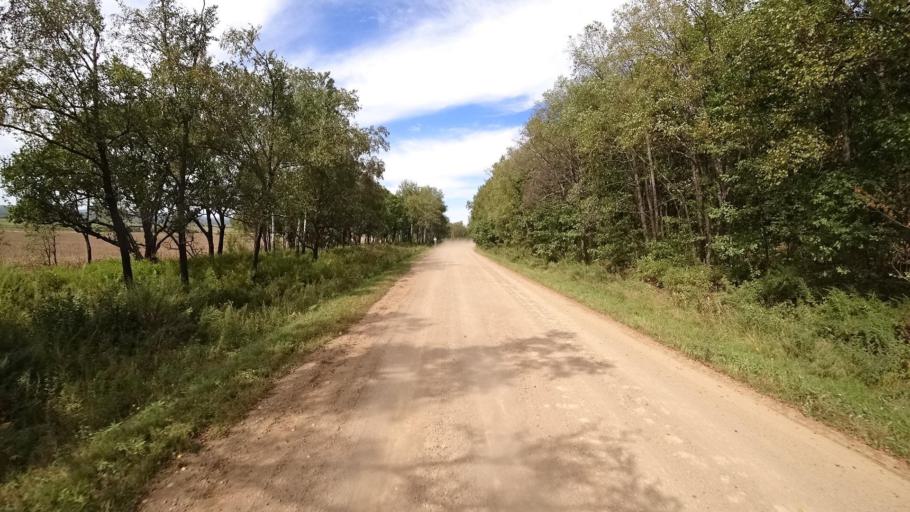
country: RU
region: Primorskiy
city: Yakovlevka
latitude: 44.5701
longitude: 133.5942
